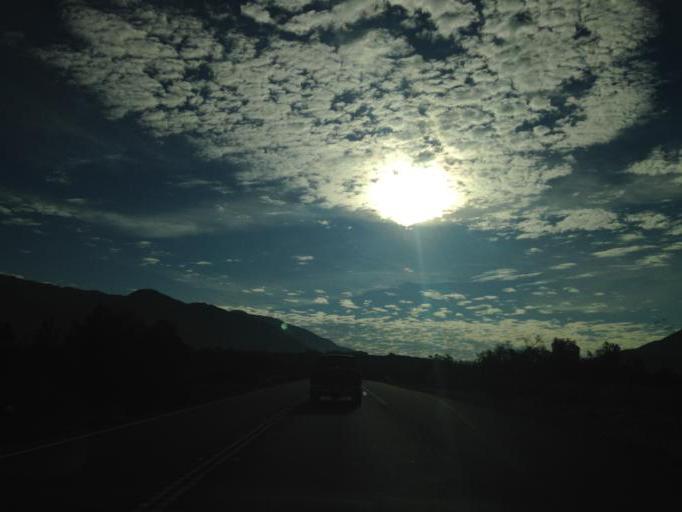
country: US
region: California
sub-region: San Diego County
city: Rainbow
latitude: 33.3622
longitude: -117.0490
